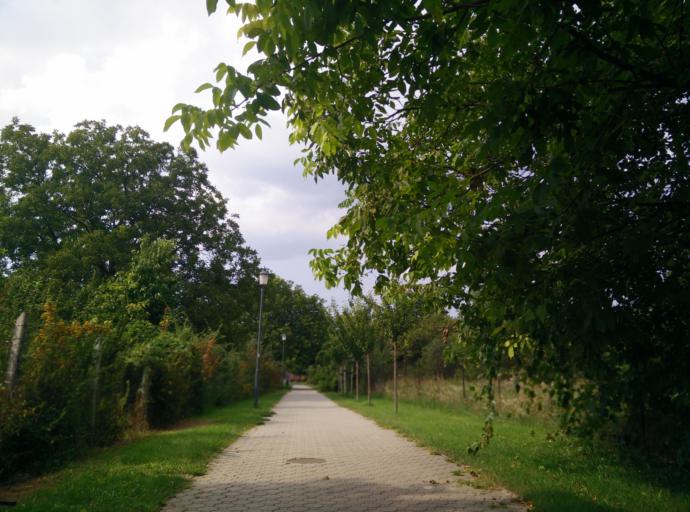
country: HU
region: Pest
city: Paty
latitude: 47.5135
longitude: 18.8288
